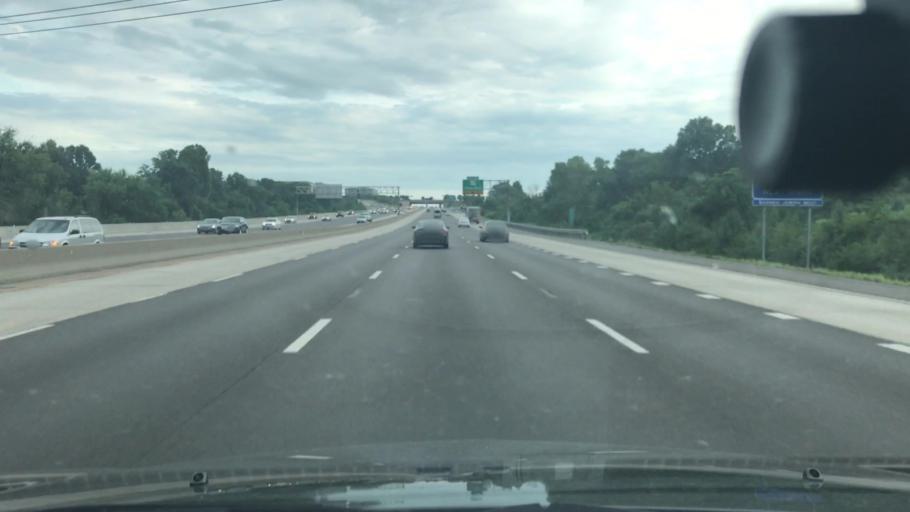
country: US
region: Missouri
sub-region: Saint Louis County
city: Creve Coeur
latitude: 38.6816
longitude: -90.4499
